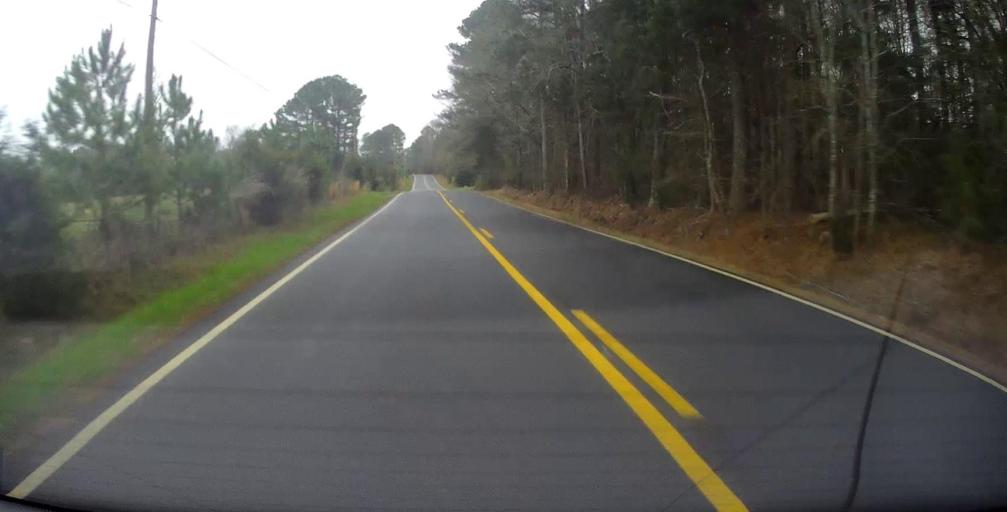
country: US
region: Georgia
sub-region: Pike County
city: Zebulon
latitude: 33.0574
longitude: -84.2763
